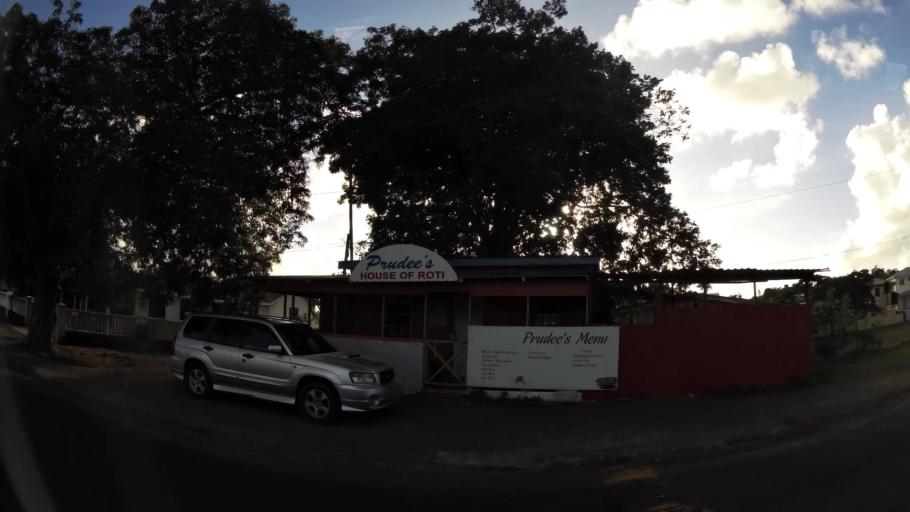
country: LC
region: Gros-Islet
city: Gros Islet
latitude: 14.0822
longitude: -60.9473
